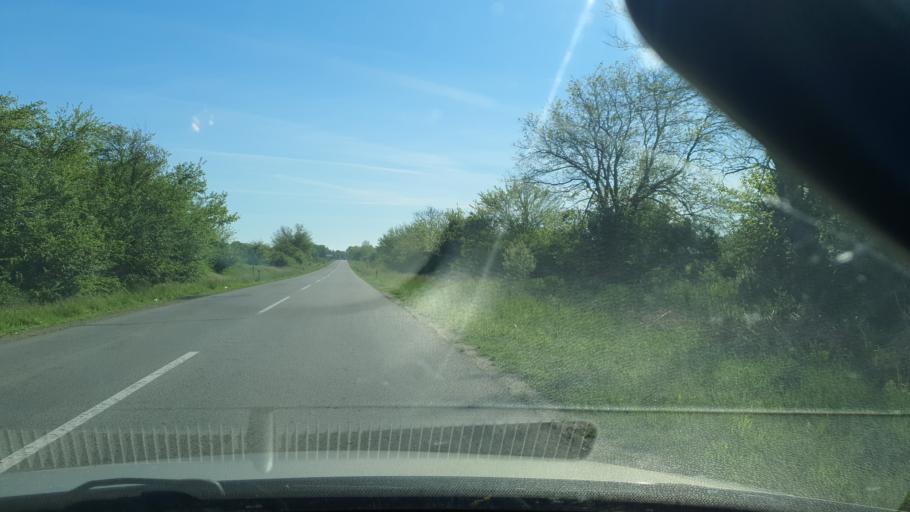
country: RS
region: Autonomna Pokrajina Vojvodina
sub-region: Juznobanatski Okrug
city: Kovin
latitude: 44.7880
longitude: 21.0386
